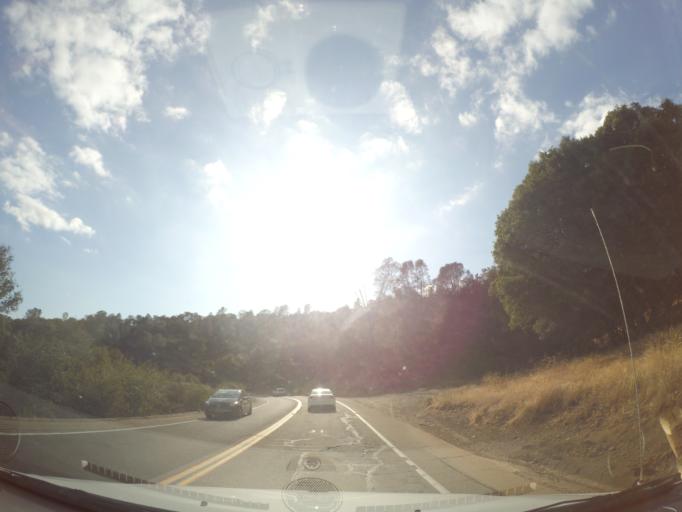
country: US
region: California
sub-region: Mariposa County
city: Mariposa
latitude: 37.5087
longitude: -119.9654
